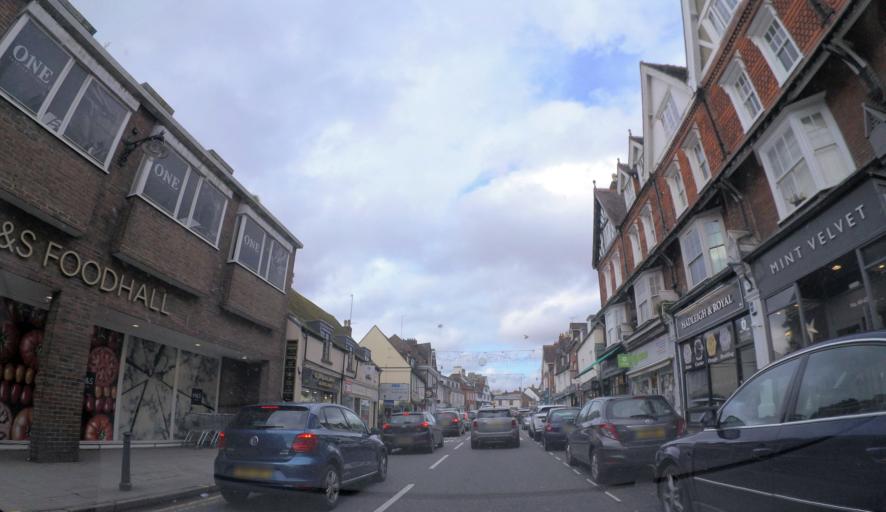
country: GB
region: England
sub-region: Surrey
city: Reigate
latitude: 51.2379
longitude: -0.2083
